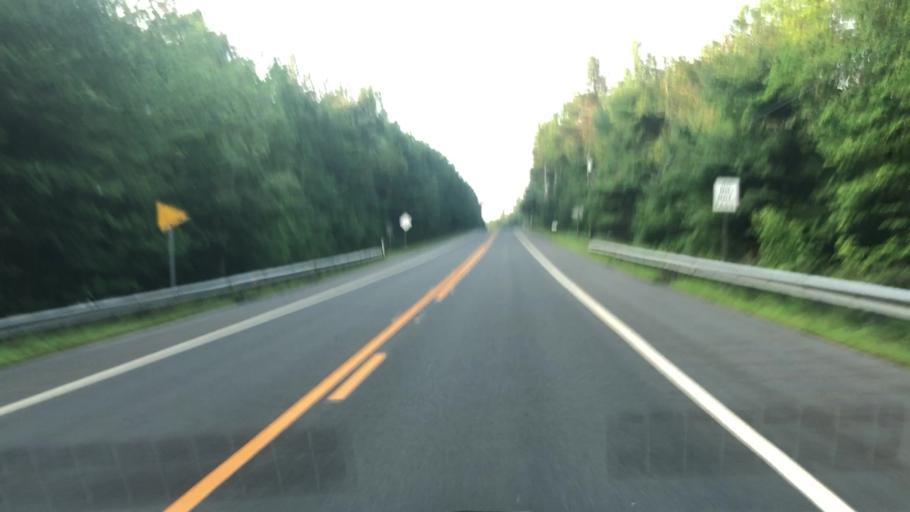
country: US
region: Massachusetts
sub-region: Franklin County
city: Ashfield
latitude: 42.4862
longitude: -72.8097
